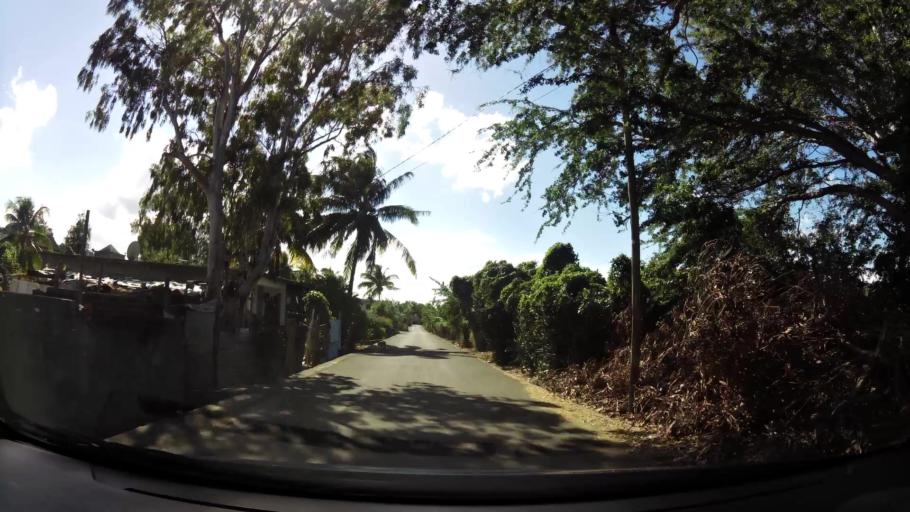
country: MU
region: Black River
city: Cascavelle
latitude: -20.2600
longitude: 57.4193
